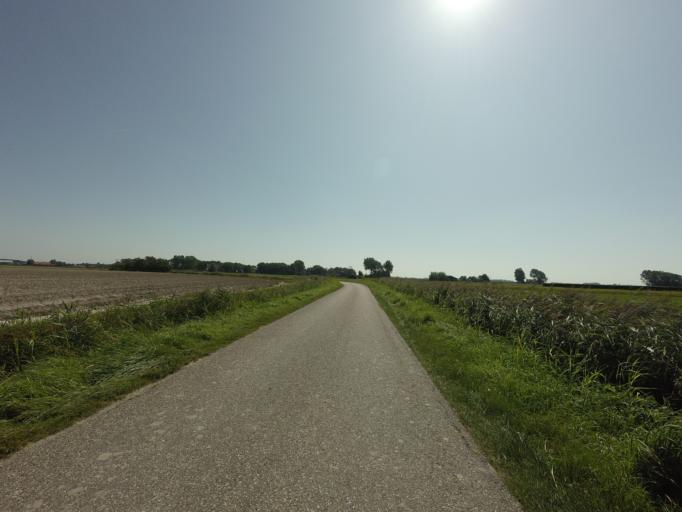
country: NL
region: Friesland
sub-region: Gemeente Dongeradeel
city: Ternaard
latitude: 53.3829
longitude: 6.0291
